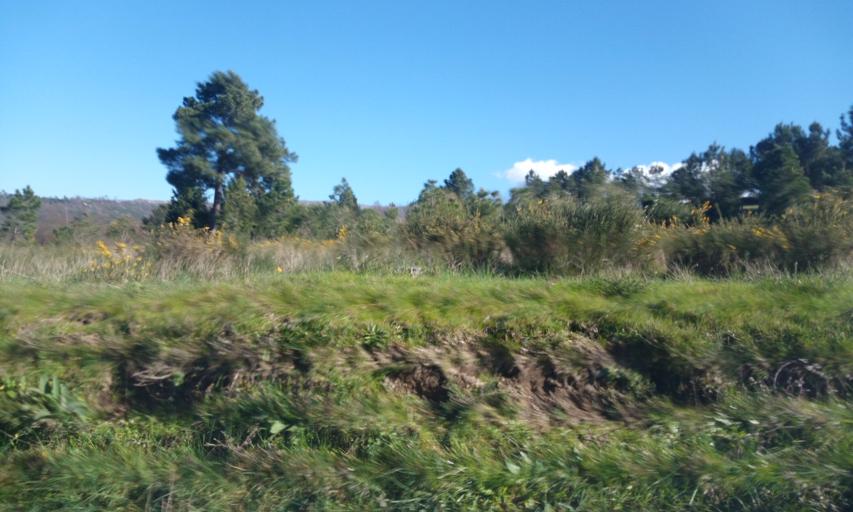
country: PT
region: Guarda
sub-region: Seia
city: Seia
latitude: 40.4729
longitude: -7.6245
